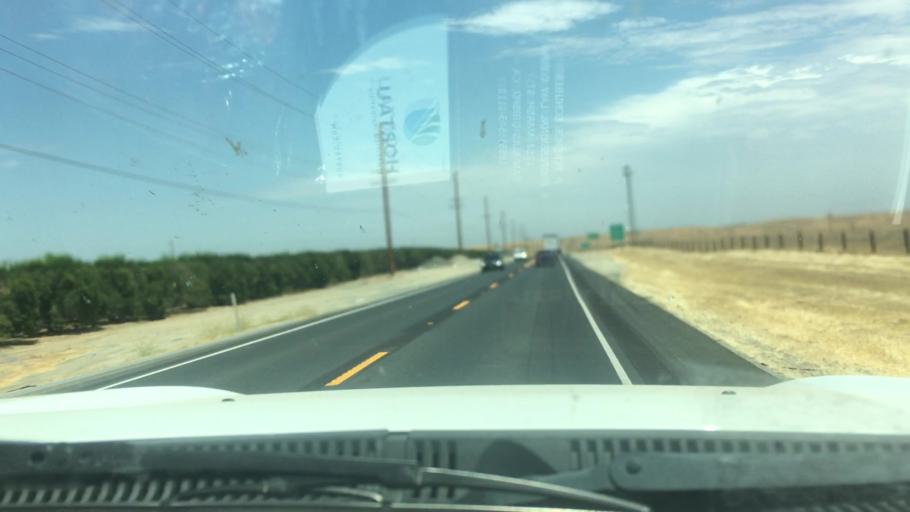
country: US
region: California
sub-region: Tulare County
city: Richgrove
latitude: 35.7570
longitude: -119.0532
